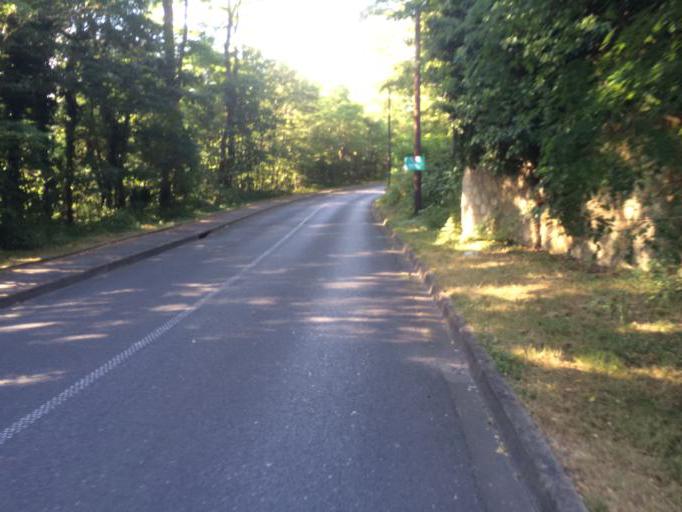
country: FR
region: Ile-de-France
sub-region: Departement de l'Essonne
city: Les Ulis
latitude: 48.6879
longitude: 2.1599
